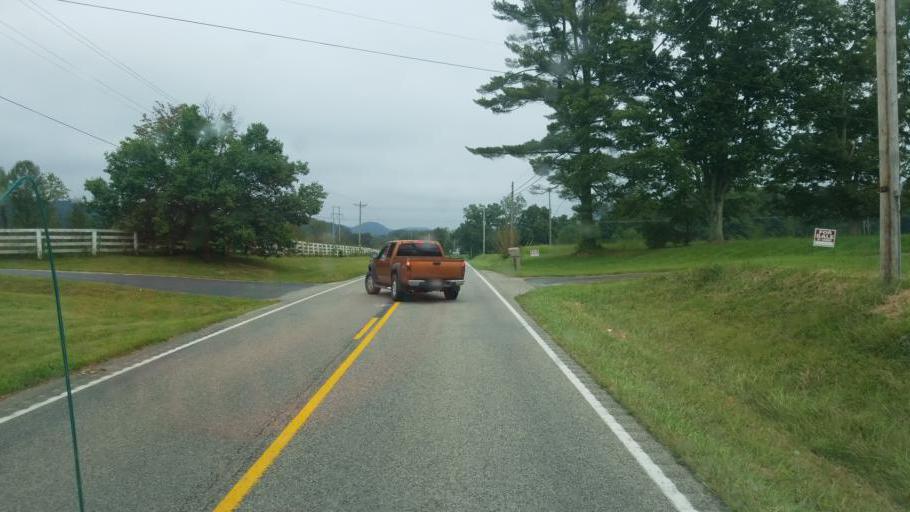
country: US
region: Kentucky
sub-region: Rowan County
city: Morehead
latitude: 38.2359
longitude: -83.4505
